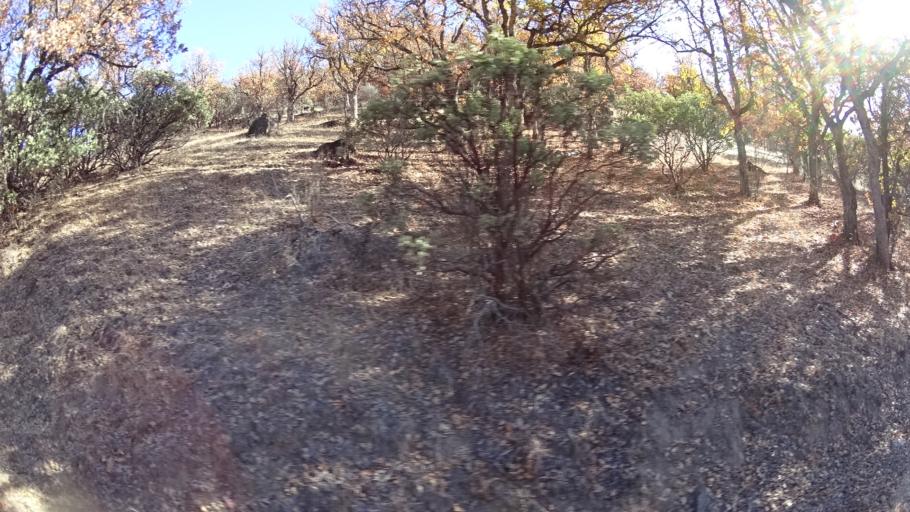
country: US
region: California
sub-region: Siskiyou County
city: Yreka
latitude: 41.8439
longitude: -122.8372
